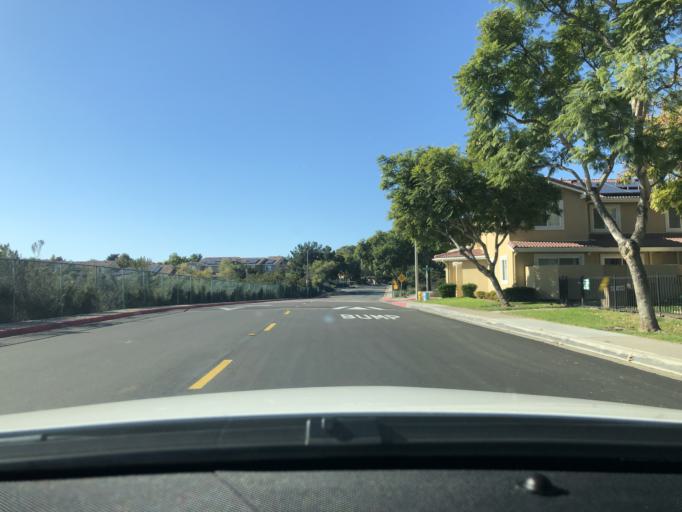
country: US
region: California
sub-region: San Diego County
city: Lemon Grove
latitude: 32.7400
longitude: -117.0605
